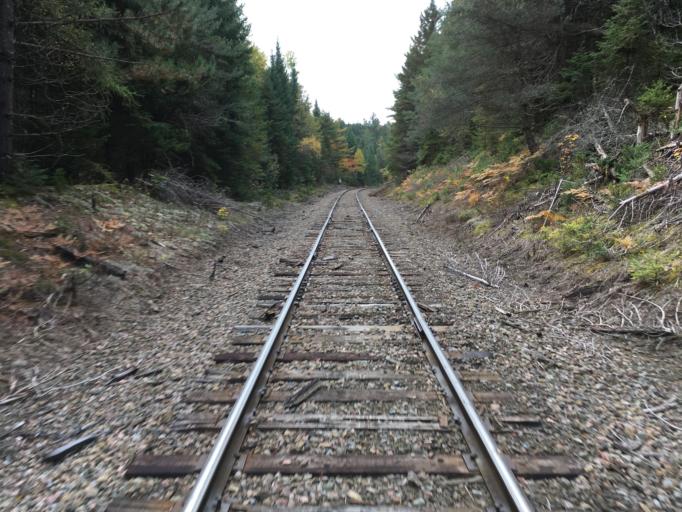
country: US
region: Vermont
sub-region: Caledonia County
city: Lyndonville
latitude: 44.6177
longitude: -71.9658
